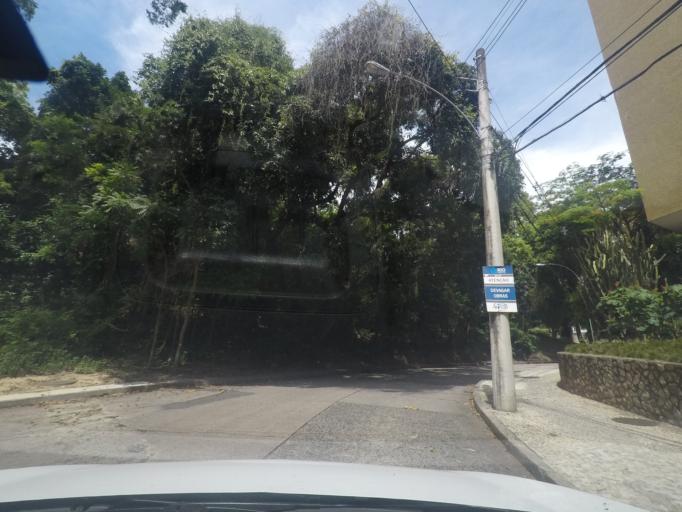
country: BR
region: Rio de Janeiro
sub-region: Rio De Janeiro
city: Rio de Janeiro
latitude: -22.9303
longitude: -43.1846
